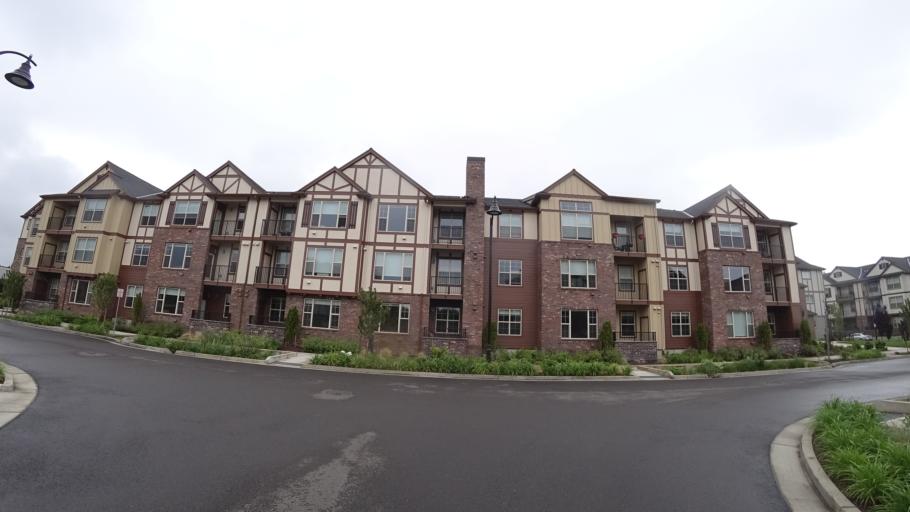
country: US
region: Oregon
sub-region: Washington County
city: Rockcreek
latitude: 45.5286
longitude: -122.8881
